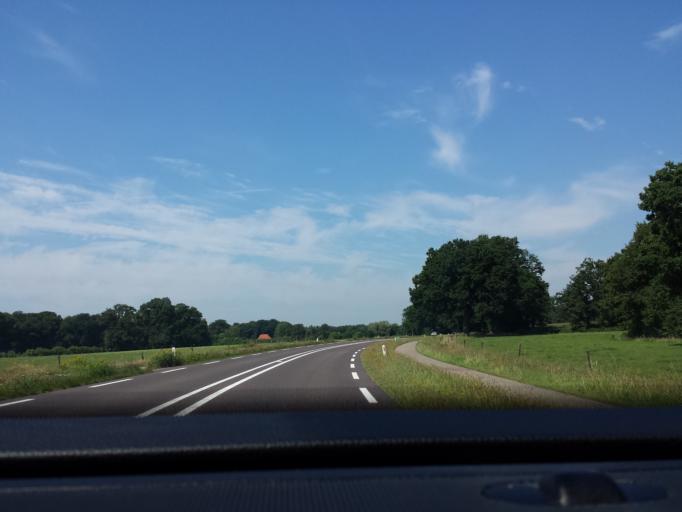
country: NL
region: Overijssel
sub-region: Gemeente Hof van Twente
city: Delden
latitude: 52.2695
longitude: 6.6943
